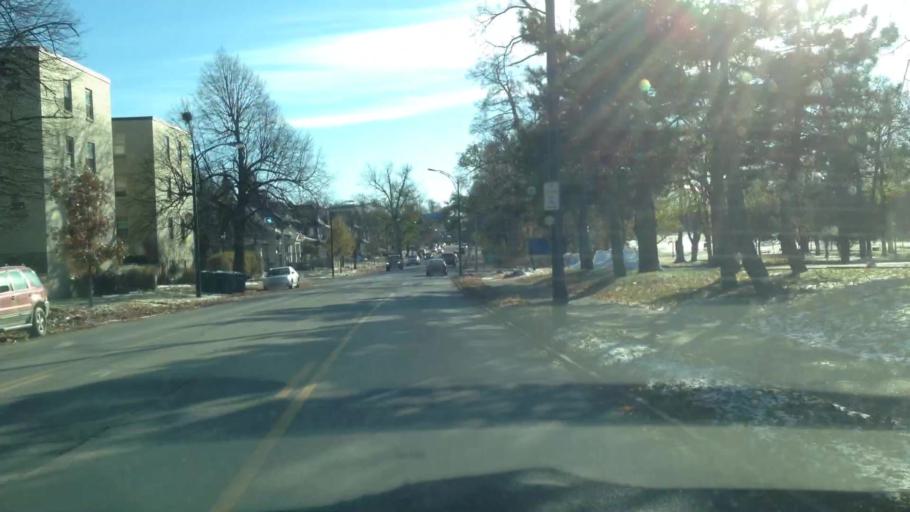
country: US
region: New York
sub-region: Erie County
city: Kenmore
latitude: 42.9367
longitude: -78.8508
